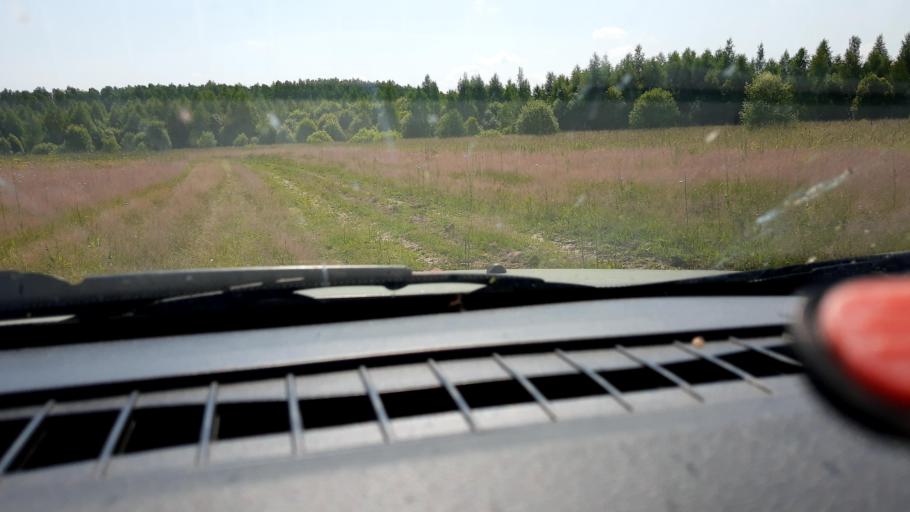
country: RU
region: Nizjnij Novgorod
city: Sharanga
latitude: 57.0464
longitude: 46.7228
